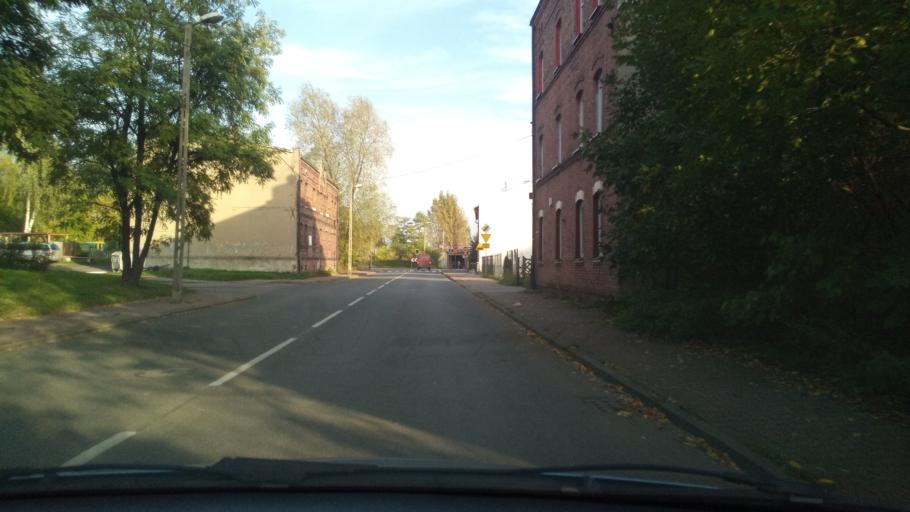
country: PL
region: Silesian Voivodeship
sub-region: Sosnowiec
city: Sosnowiec
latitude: 50.2642
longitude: 19.1056
